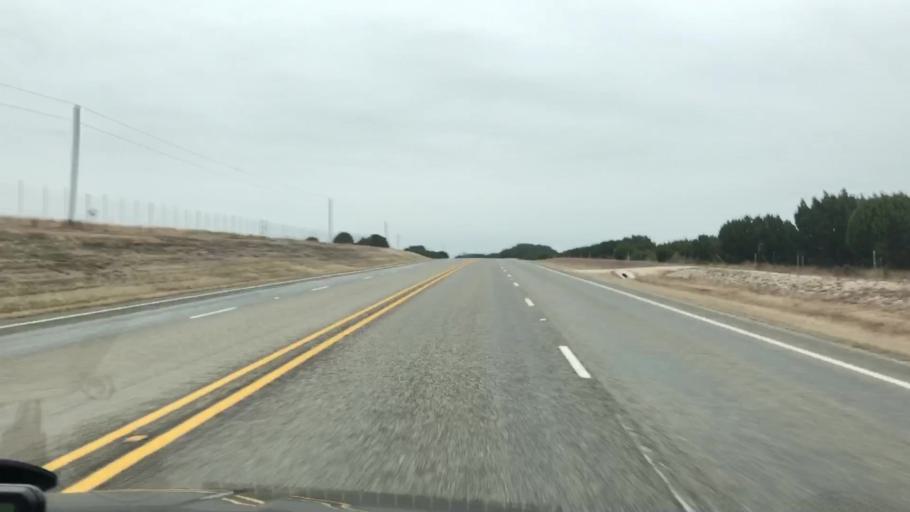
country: US
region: Texas
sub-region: Lampasas County
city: Lampasas
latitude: 31.1845
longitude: -98.1725
